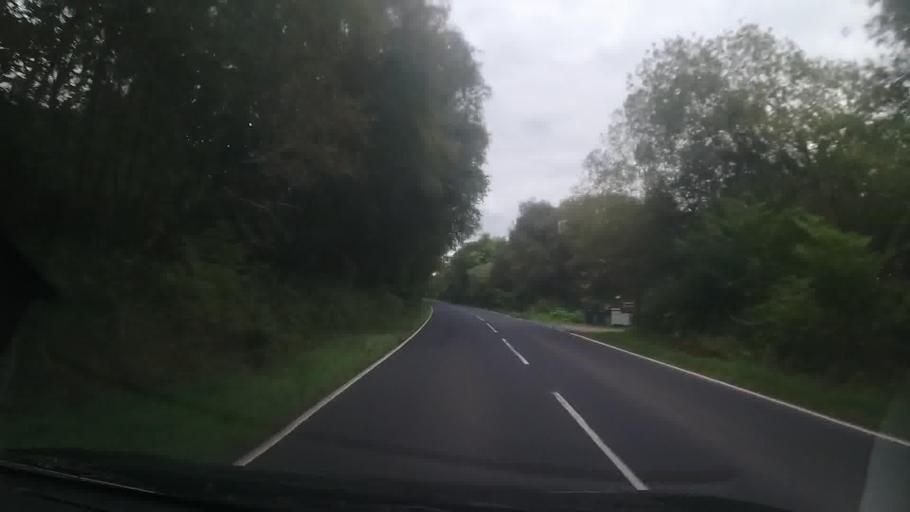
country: GB
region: Scotland
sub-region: Argyll and Bute
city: Garelochhead
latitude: 56.2029
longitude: -5.0619
